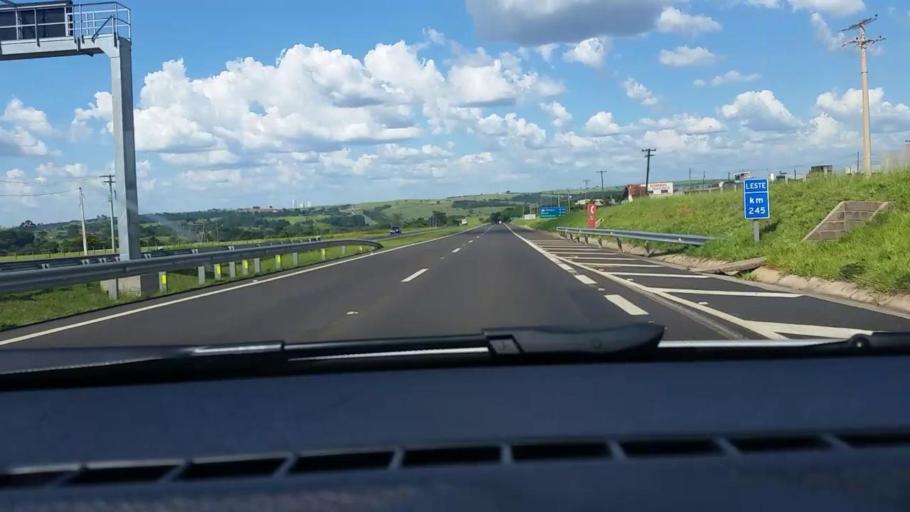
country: BR
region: Sao Paulo
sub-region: Bauru
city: Bauru
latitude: -22.4197
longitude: -49.1154
